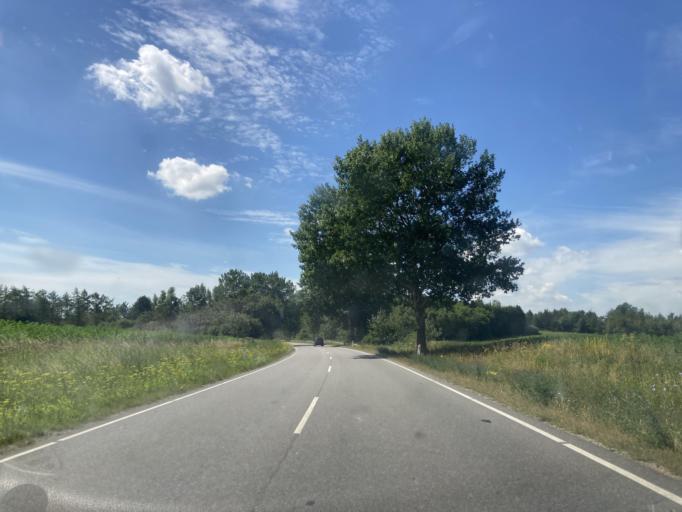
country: DK
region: Zealand
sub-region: Koge Kommune
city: Ejby
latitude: 55.4822
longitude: 12.0778
